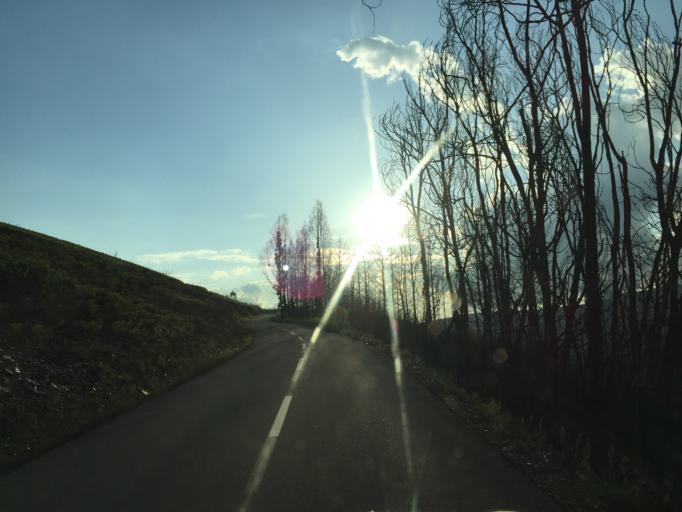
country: PT
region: Coimbra
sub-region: Pampilhosa da Serra
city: Pampilhosa da Serra
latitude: 40.1336
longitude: -7.9946
